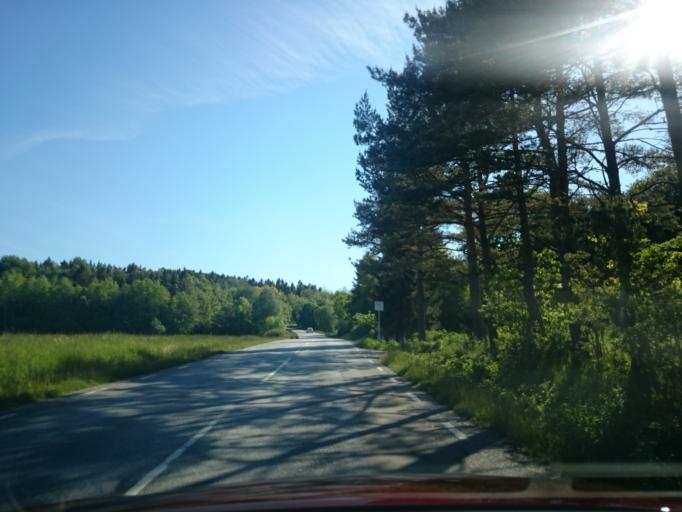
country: SE
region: Vaestra Goetaland
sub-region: Lysekils Kommun
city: Lysekil
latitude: 58.2589
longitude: 11.5320
